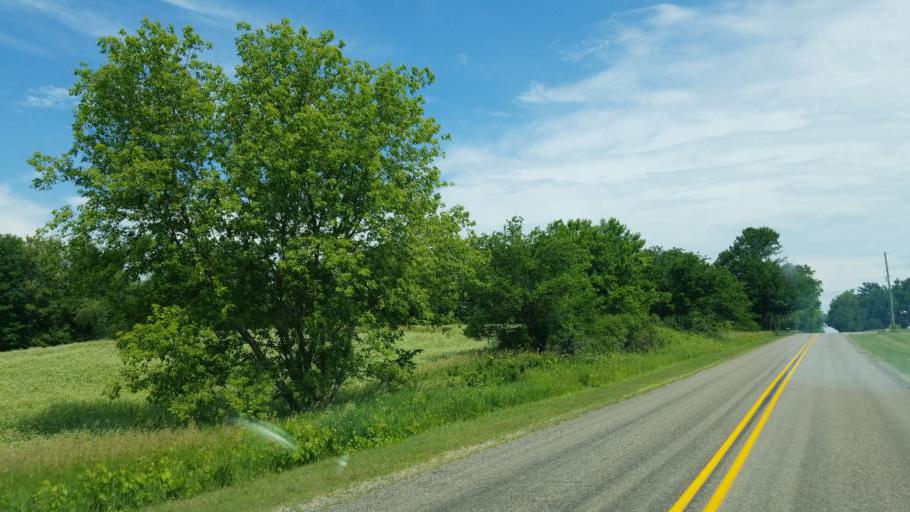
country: US
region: Michigan
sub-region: Barry County
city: Nashville
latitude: 42.6677
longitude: -85.0344
